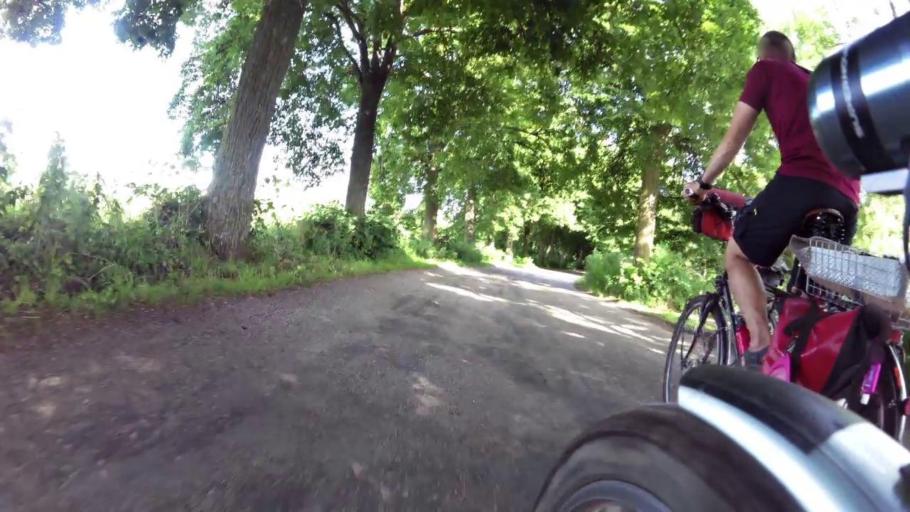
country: PL
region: West Pomeranian Voivodeship
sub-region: Powiat lobeski
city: Radowo Male
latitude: 53.5824
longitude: 15.4582
